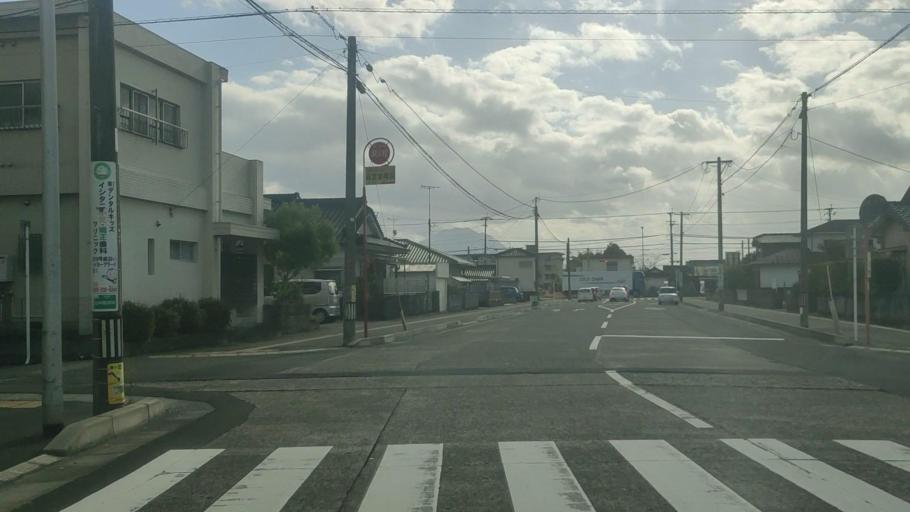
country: JP
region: Kagoshima
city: Kajiki
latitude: 31.7357
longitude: 130.6701
